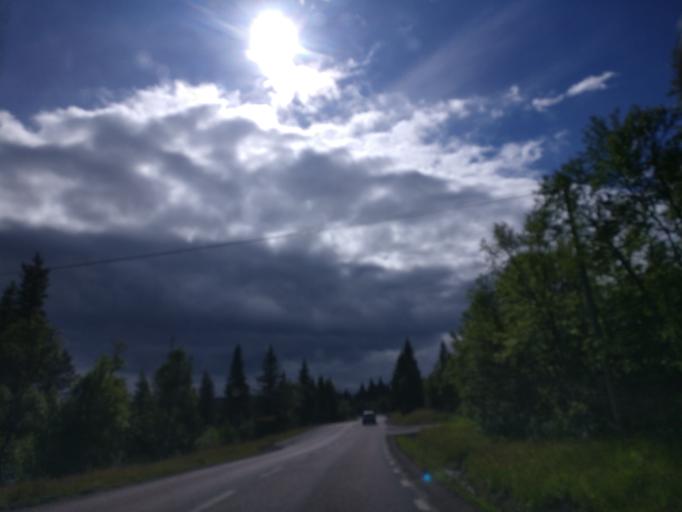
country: SE
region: Dalarna
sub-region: Malung-Saelens kommun
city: Malung
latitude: 61.1616
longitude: 13.1430
